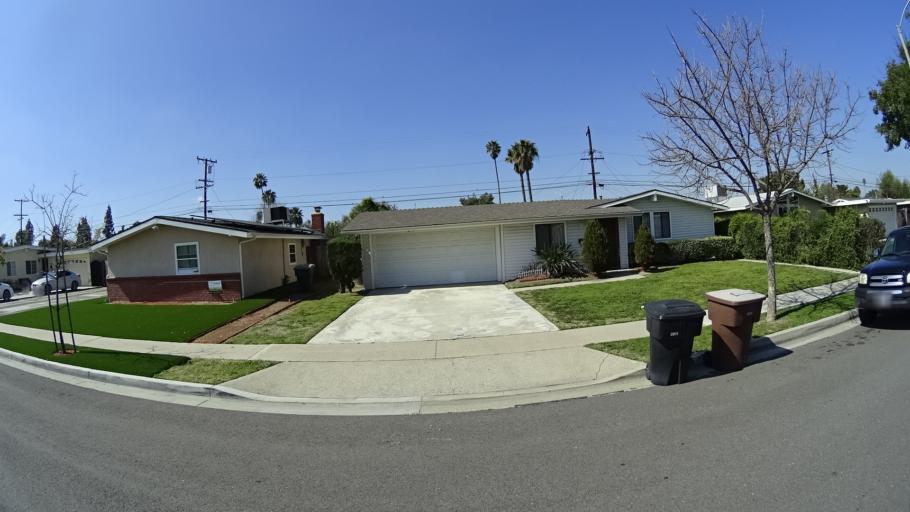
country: US
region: California
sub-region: Orange County
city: Fullerton
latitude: 33.8447
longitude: -117.9508
